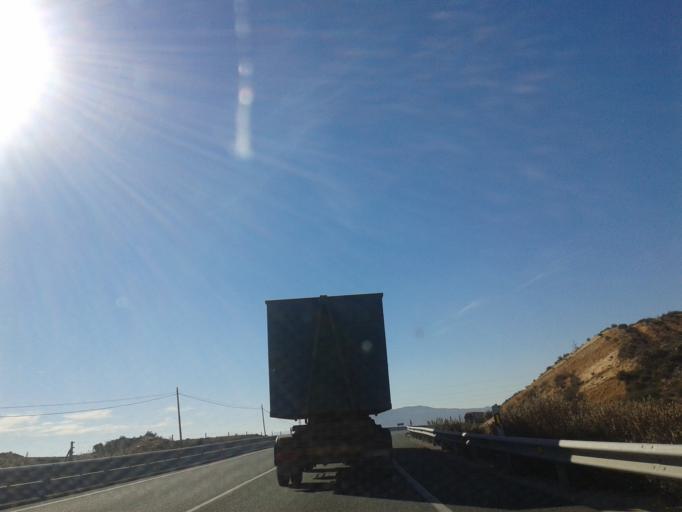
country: ES
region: Castille-La Mancha
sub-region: Provincia de Albacete
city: Caudete
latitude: 38.7269
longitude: -0.9430
